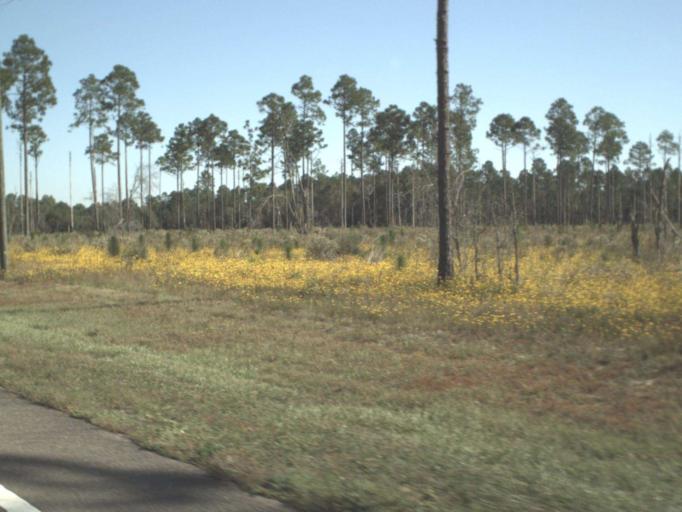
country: US
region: Florida
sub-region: Walton County
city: Freeport
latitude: 30.5087
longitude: -85.9270
